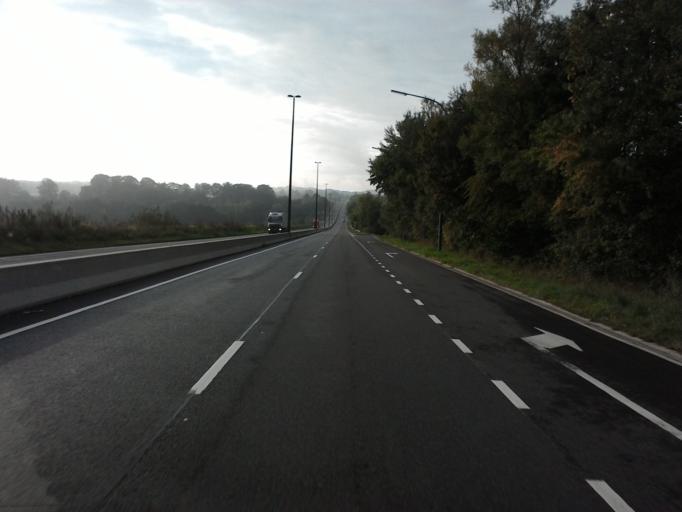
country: BE
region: Wallonia
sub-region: Province du Luxembourg
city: Attert
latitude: 49.7507
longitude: 5.7799
